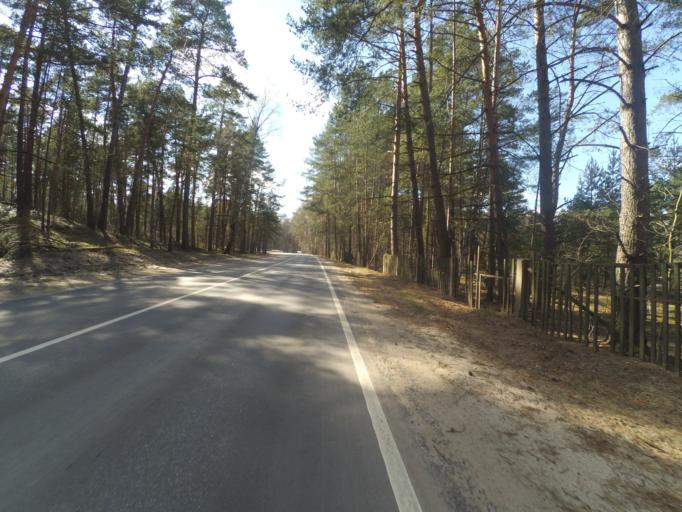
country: RU
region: Moskovskaya
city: Stupino
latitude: 54.8498
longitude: 38.0566
